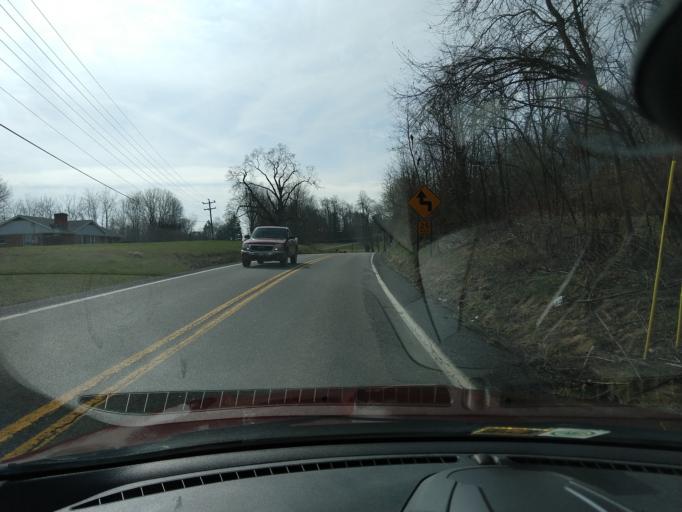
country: US
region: West Virginia
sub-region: Greenbrier County
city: Lewisburg
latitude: 37.8695
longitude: -80.4107
